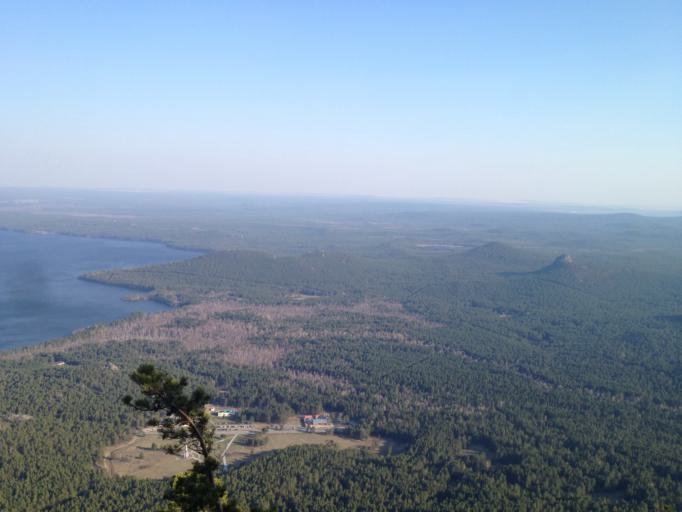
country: KZ
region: Soltustik Qazaqstan
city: Burabay
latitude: 53.0899
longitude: 70.2268
